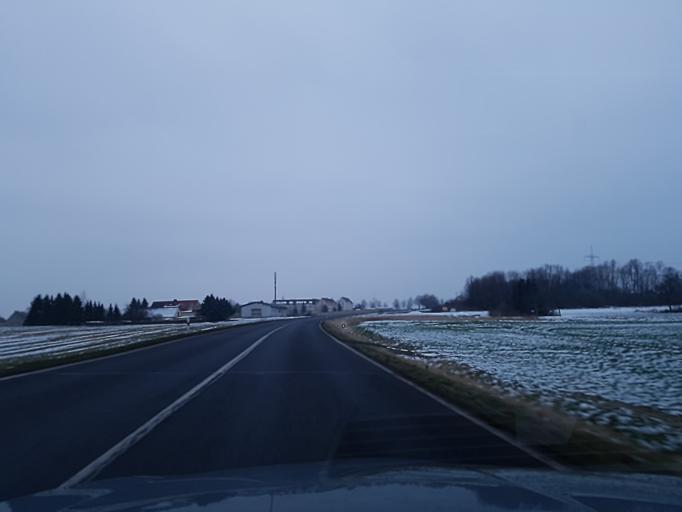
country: DE
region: Saxony
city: Ostrau
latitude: 51.2099
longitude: 13.1581
